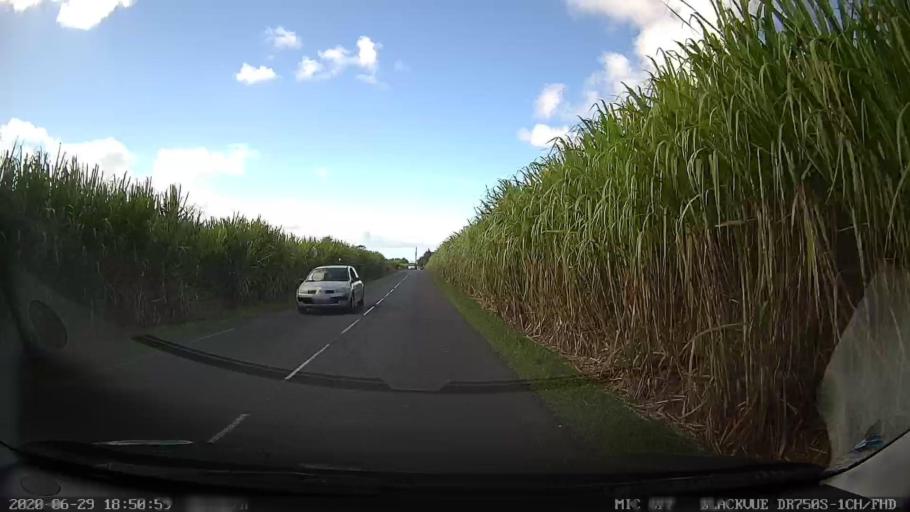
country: RE
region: Reunion
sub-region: Reunion
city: Bras-Panon
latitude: -20.9886
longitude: 55.6584
